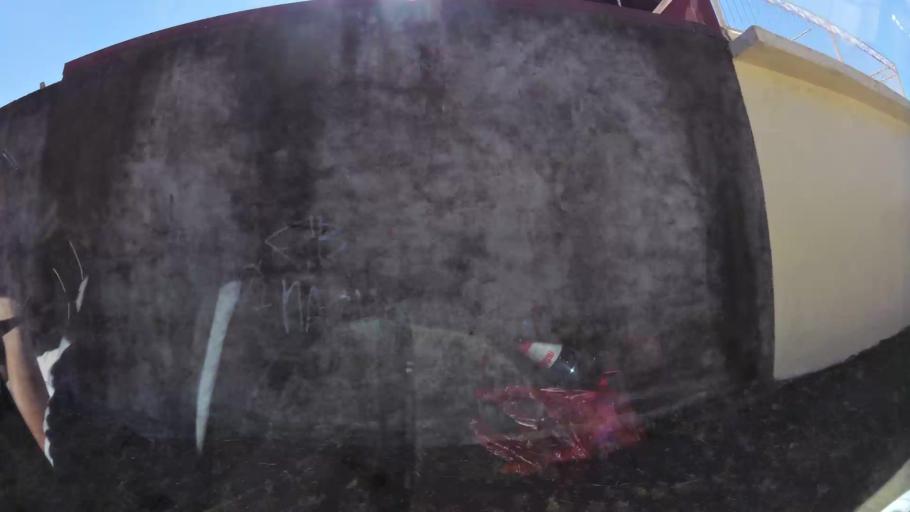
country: CL
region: Biobio
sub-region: Provincia de Concepcion
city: Talcahuano
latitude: -36.7624
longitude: -73.0921
